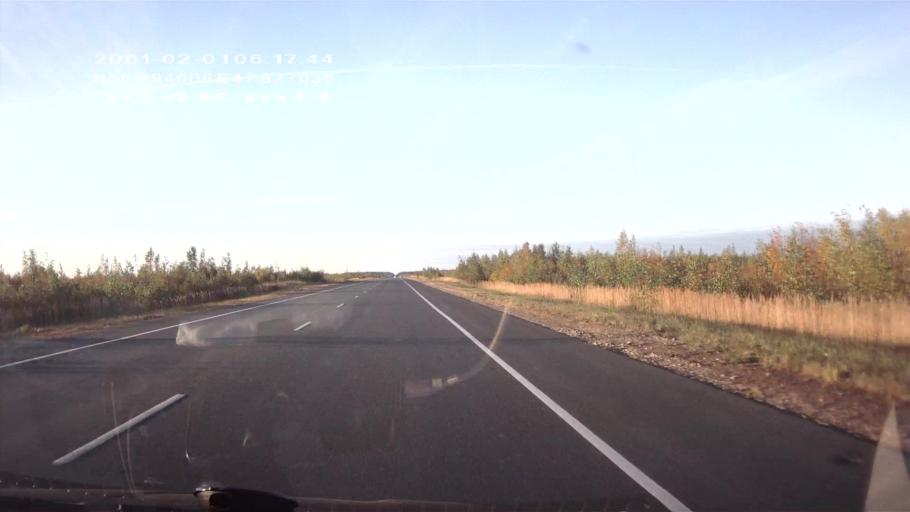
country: RU
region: Mariy-El
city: Medvedevo
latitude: 56.3934
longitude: 47.8269
